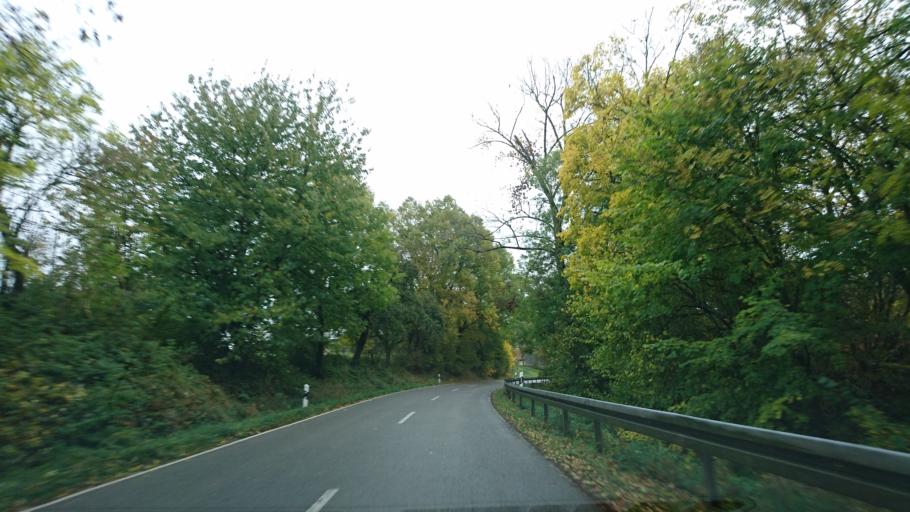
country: DE
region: Bavaria
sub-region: Regierungsbezirk Mittelfranken
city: Thalmassing
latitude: 49.1240
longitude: 11.1892
